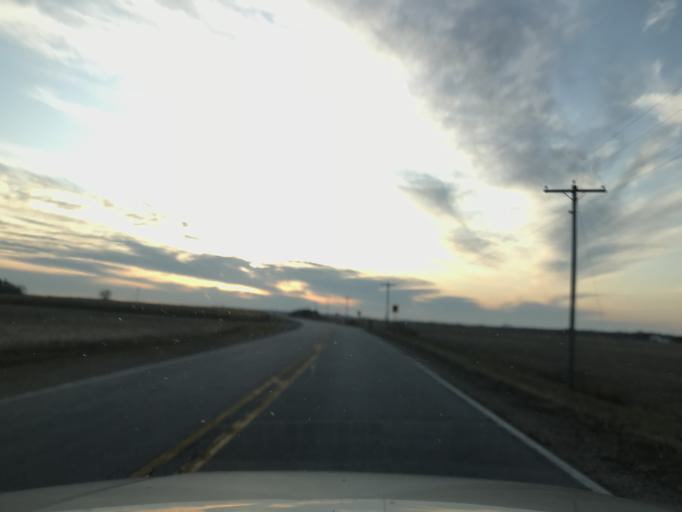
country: US
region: Illinois
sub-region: Warren County
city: Monmouth
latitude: 41.0245
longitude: -90.7788
